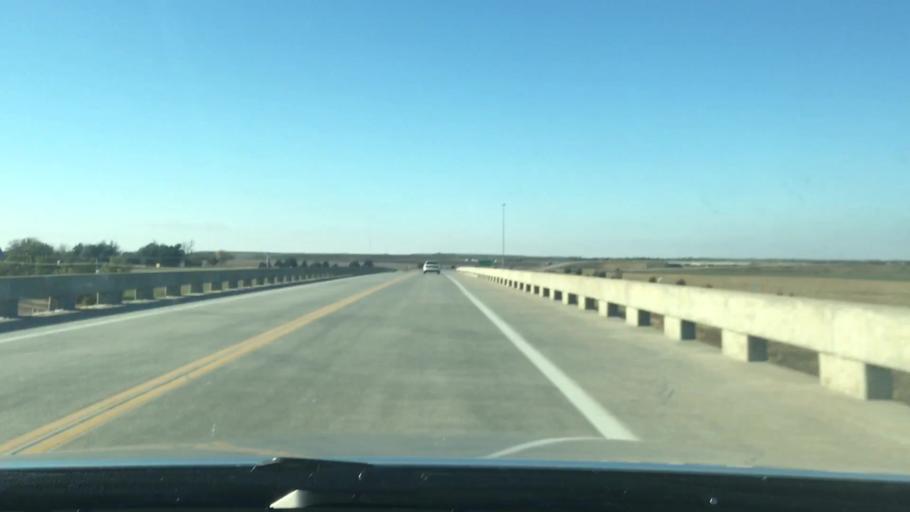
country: US
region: Kansas
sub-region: Reno County
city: South Hutchinson
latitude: 38.0276
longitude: -97.9803
